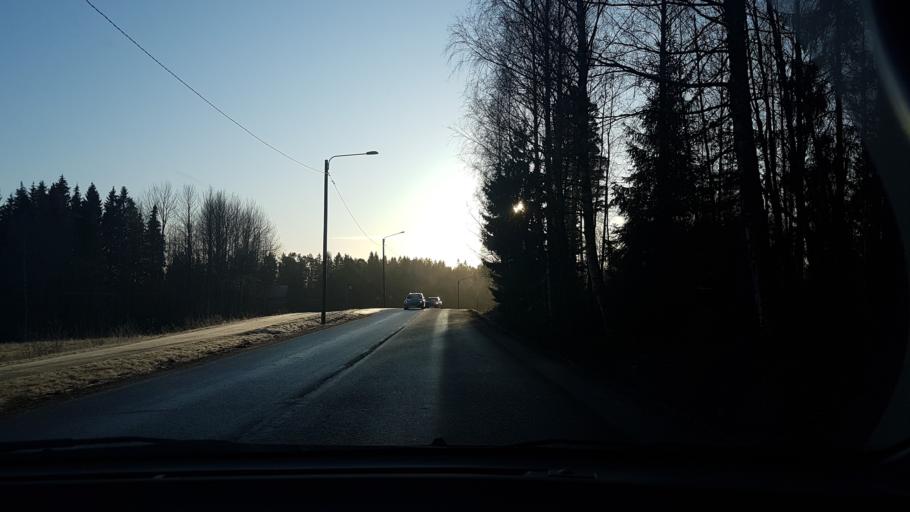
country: FI
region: Uusimaa
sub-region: Helsinki
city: Tuusula
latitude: 60.3774
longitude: 24.9745
